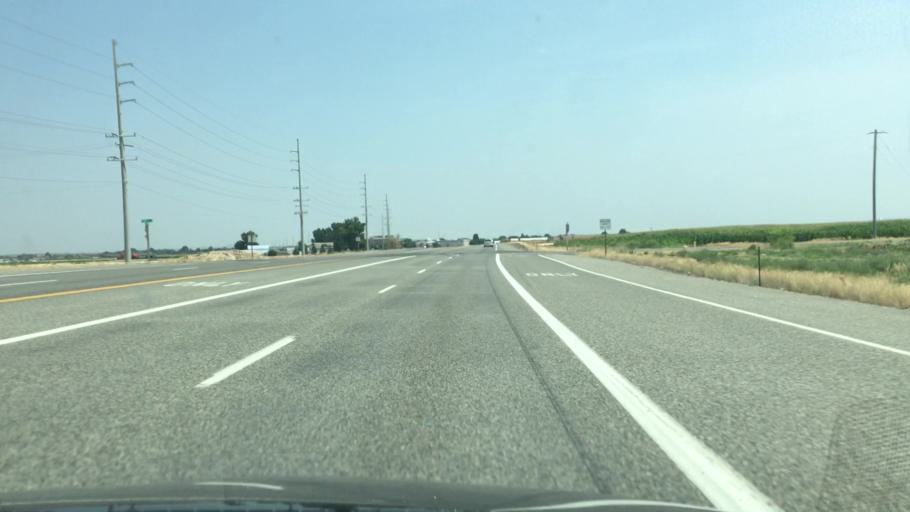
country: US
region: Idaho
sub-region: Twin Falls County
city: Twin Falls
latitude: 42.5929
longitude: -114.5169
